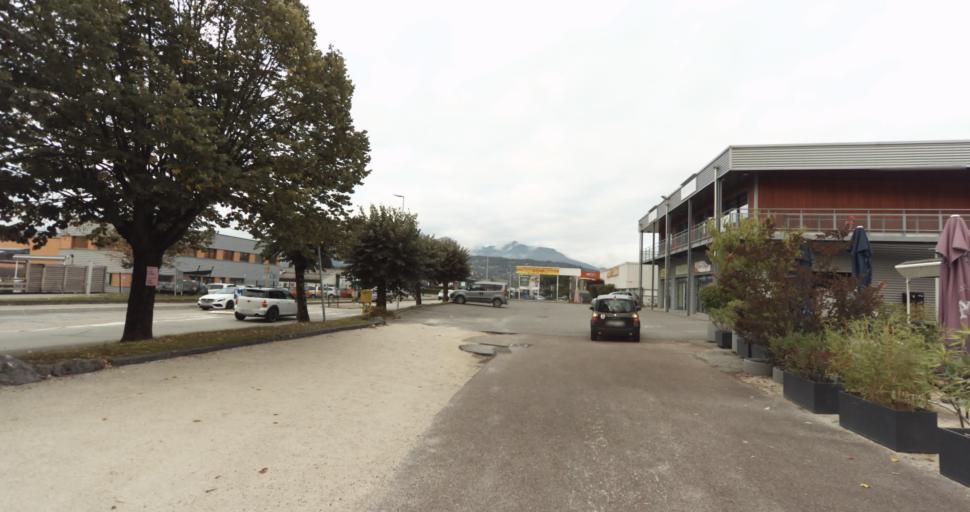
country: FR
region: Rhone-Alpes
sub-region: Departement de la Savoie
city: La Ravoire
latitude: 45.5670
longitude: 5.9707
